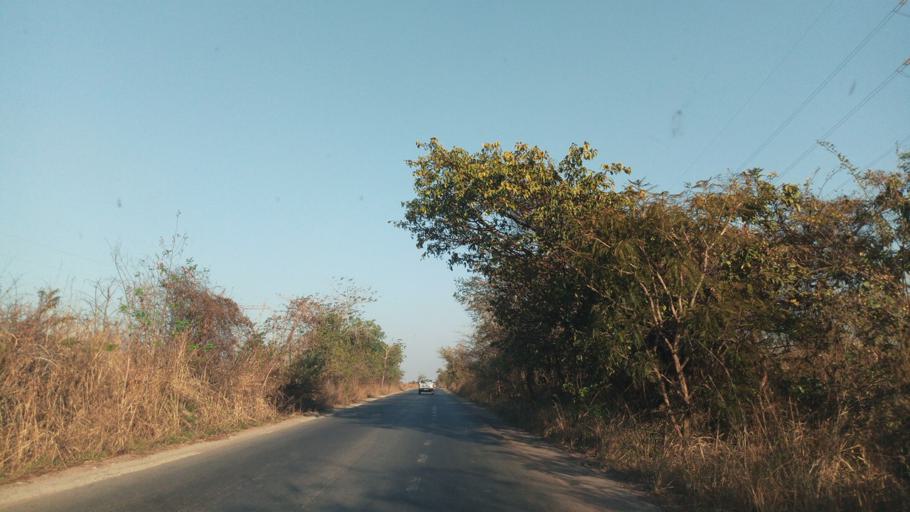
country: CD
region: Katanga
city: Likasi
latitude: -11.1051
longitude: 27.0173
